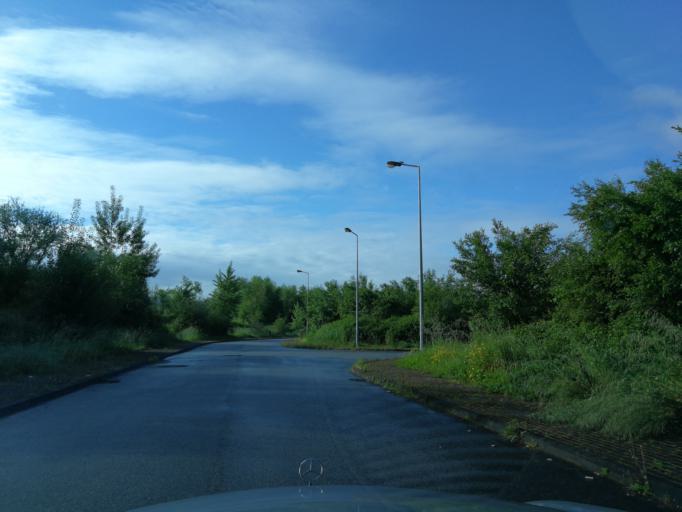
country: PT
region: Braga
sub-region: Braga
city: Braga
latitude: 41.5682
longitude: -8.4481
